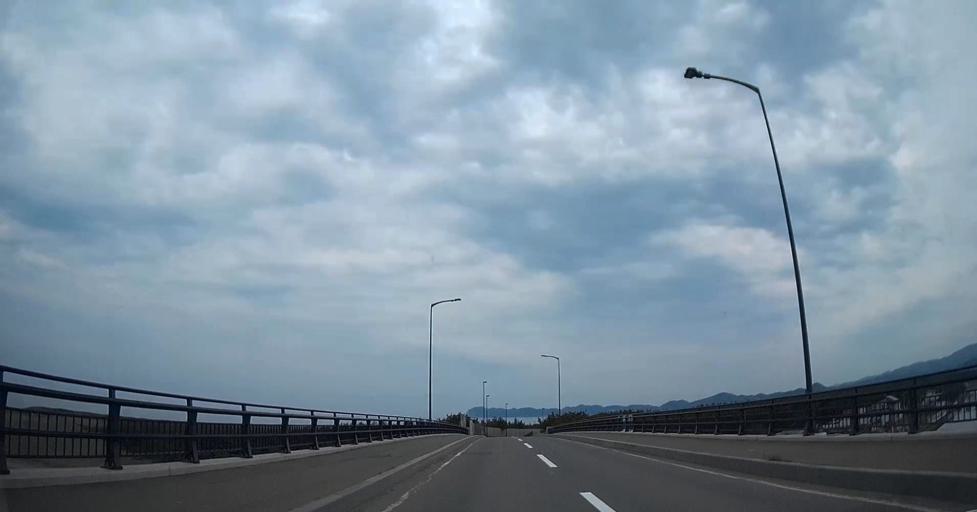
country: JP
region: Aomori
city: Shimokizukuri
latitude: 41.0391
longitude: 140.3264
